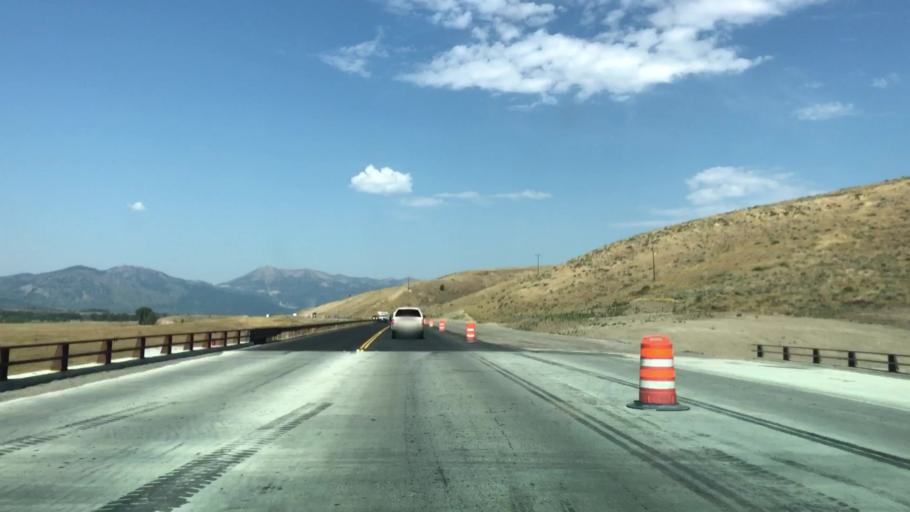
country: US
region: Wyoming
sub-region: Teton County
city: South Park
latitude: 43.4035
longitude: -110.7570
